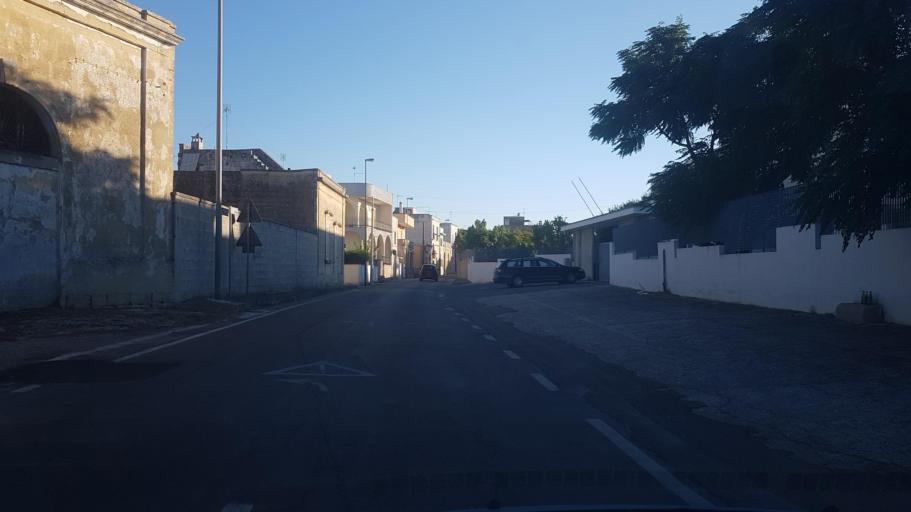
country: IT
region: Apulia
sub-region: Provincia di Lecce
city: Struda
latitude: 40.3224
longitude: 18.2848
